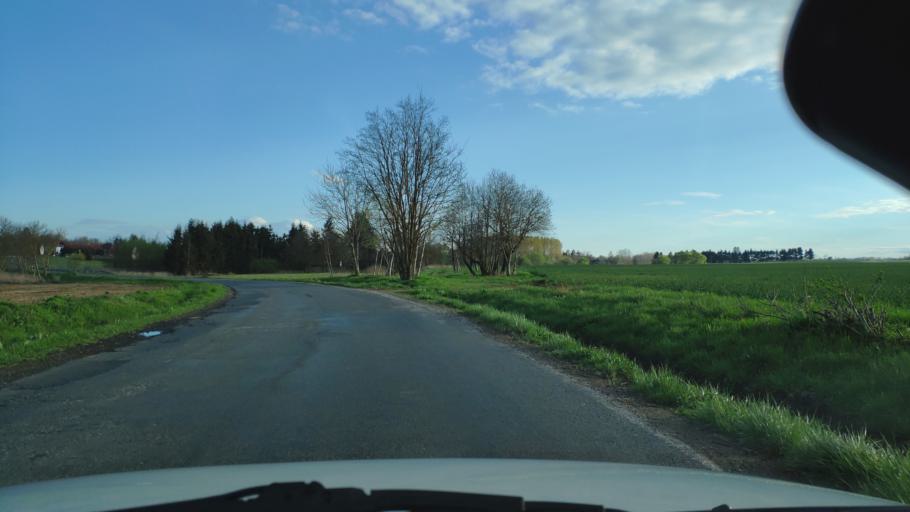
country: HU
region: Zala
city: Zalakomar
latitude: 46.4601
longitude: 17.1252
